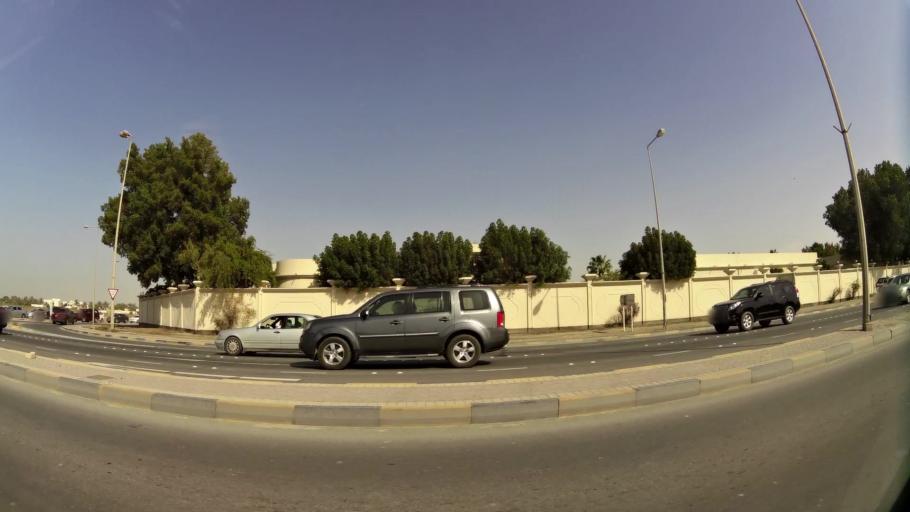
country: BH
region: Central Governorate
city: Madinat Hamad
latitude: 26.1816
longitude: 50.4657
